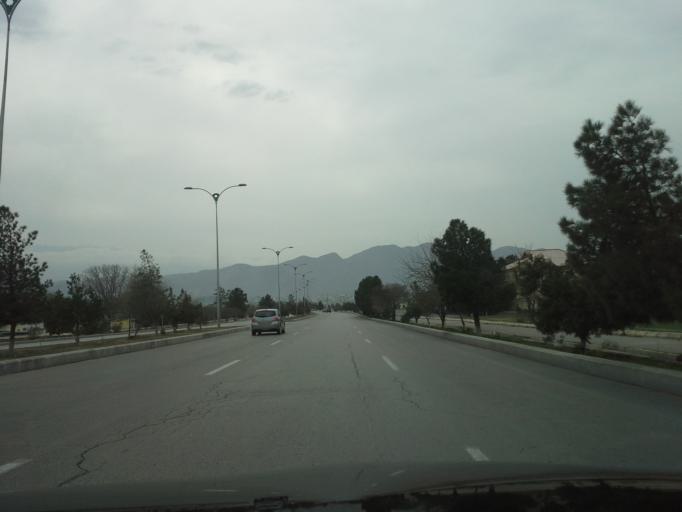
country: TM
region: Ahal
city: Abadan
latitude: 37.9705
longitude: 58.2338
